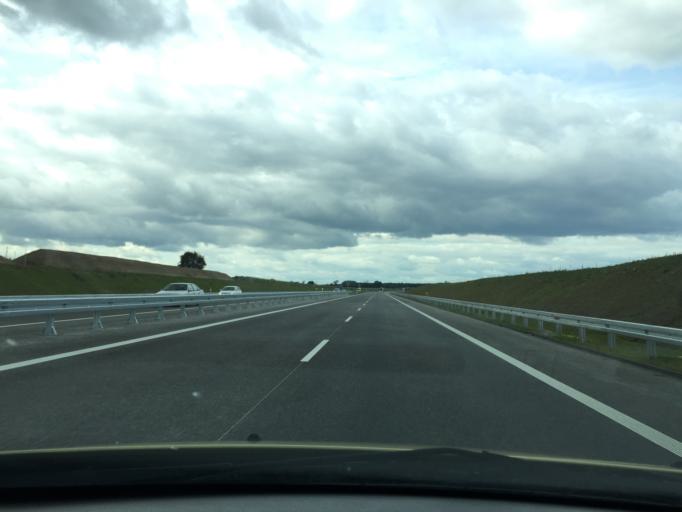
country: PL
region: Greater Poland Voivodeship
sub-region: Powiat jarocinski
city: Jarocin
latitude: 51.9824
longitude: 17.5176
